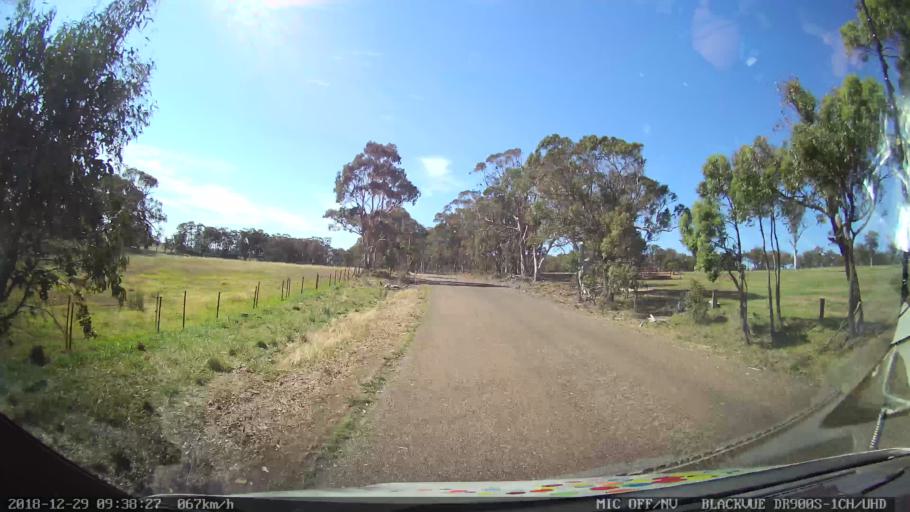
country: AU
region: New South Wales
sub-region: Upper Lachlan Shire
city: Crookwell
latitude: -34.6470
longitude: 149.3762
